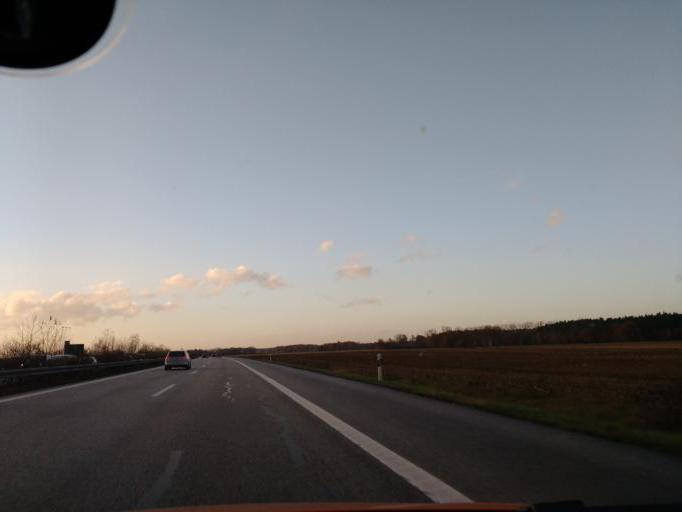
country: DE
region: Mecklenburg-Vorpommern
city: Sulstorf
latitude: 53.4670
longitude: 11.3328
